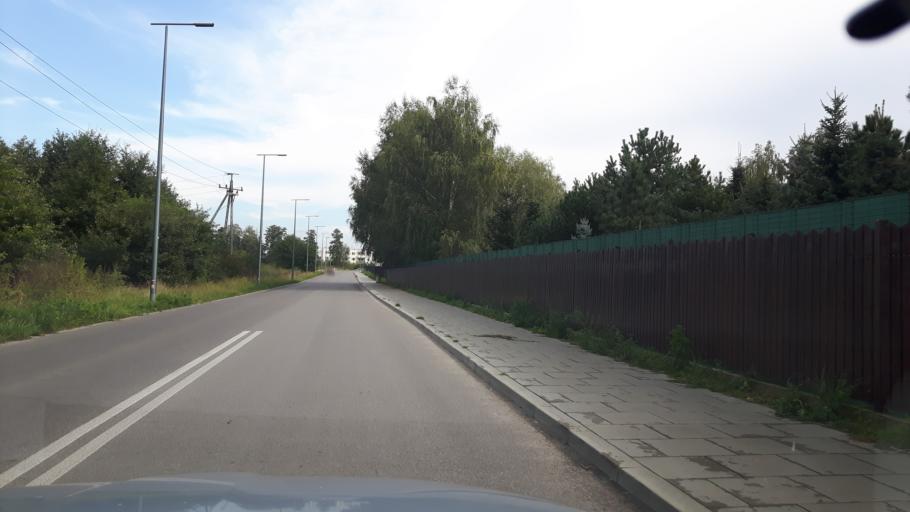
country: PL
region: Masovian Voivodeship
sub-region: Warszawa
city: Targowek
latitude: 52.3161
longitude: 21.0510
